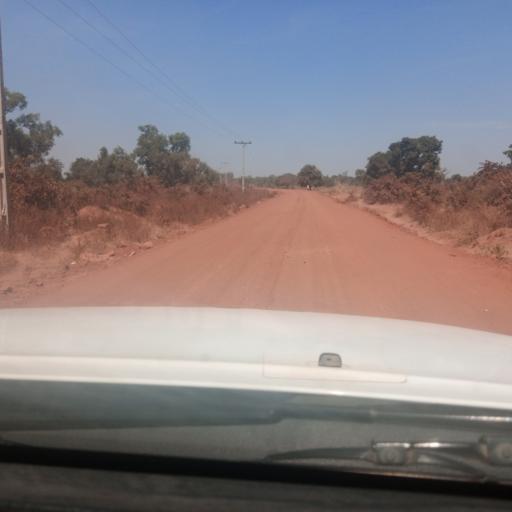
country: NG
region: Adamawa
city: Yola
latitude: 9.2047
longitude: 12.8778
